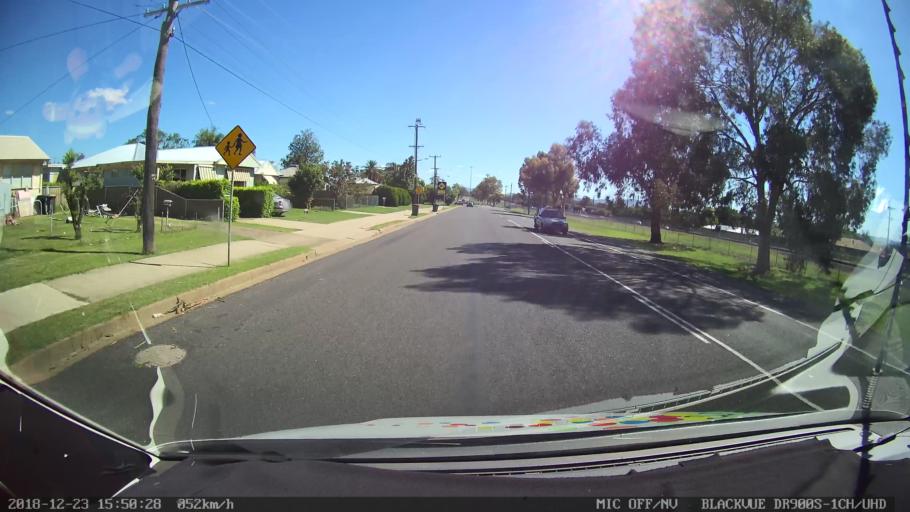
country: AU
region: New South Wales
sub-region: Tamworth Municipality
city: South Tamworth
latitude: -31.1063
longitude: 150.9006
